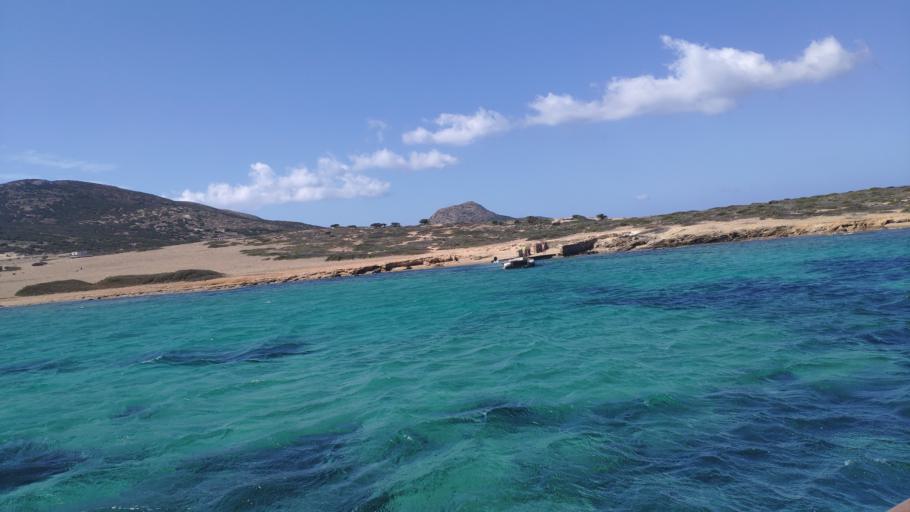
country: GR
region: South Aegean
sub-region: Nomos Kykladon
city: Antiparos
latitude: 36.9732
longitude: 25.0179
